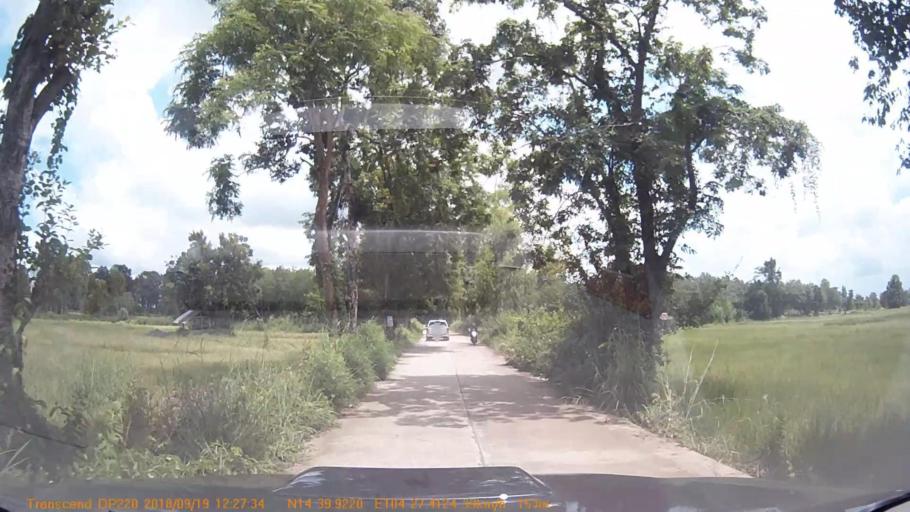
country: TH
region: Sisaket
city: Khun Han
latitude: 14.6655
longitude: 104.4573
